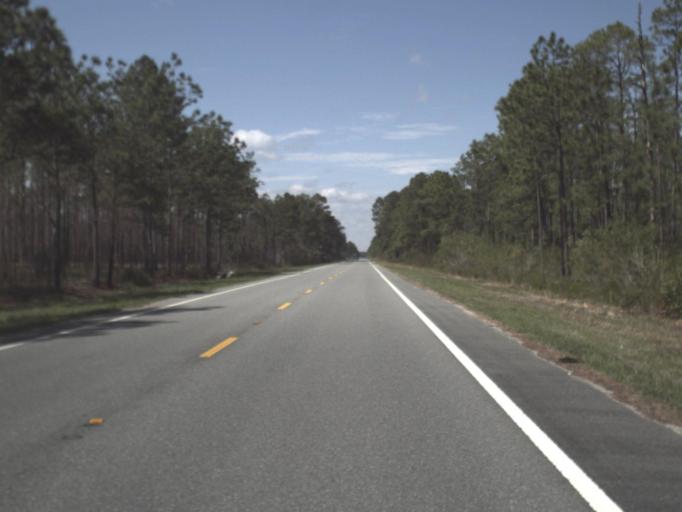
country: US
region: Florida
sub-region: Gadsden County
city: Midway
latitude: 30.3433
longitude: -84.4973
